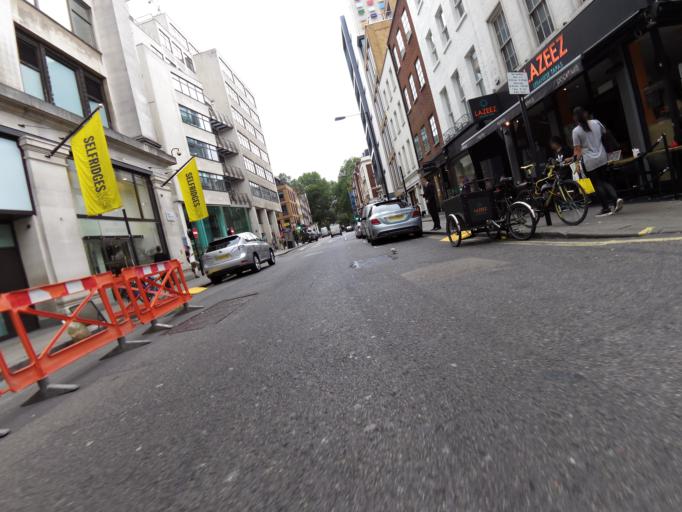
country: GB
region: England
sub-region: Greater London
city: Camden Town
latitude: 51.5152
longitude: -0.1519
